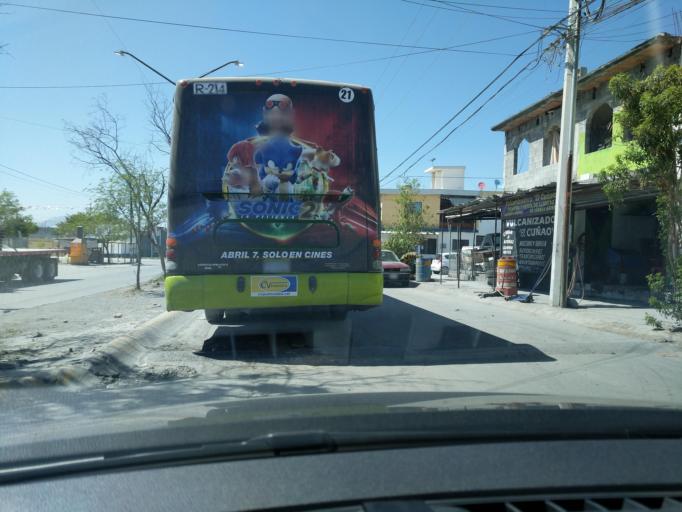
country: MX
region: Nuevo Leon
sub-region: Juarez
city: San Antonio
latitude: 25.6499
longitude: -100.0723
